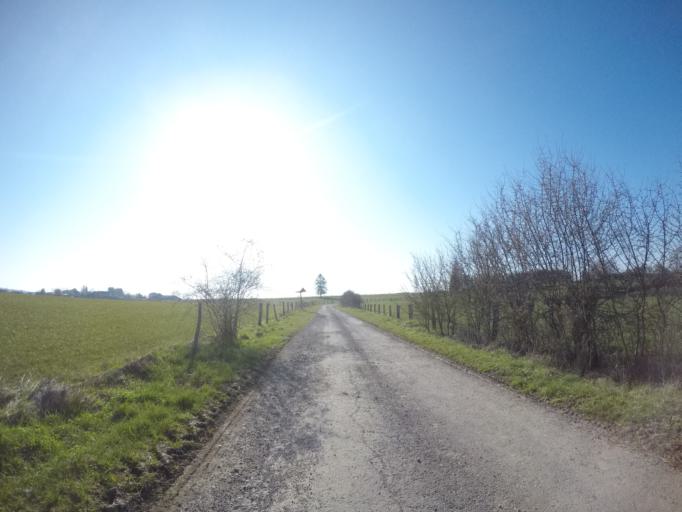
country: BE
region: Wallonia
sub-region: Province du Luxembourg
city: Habay-la-Vieille
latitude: 49.7144
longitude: 5.5729
